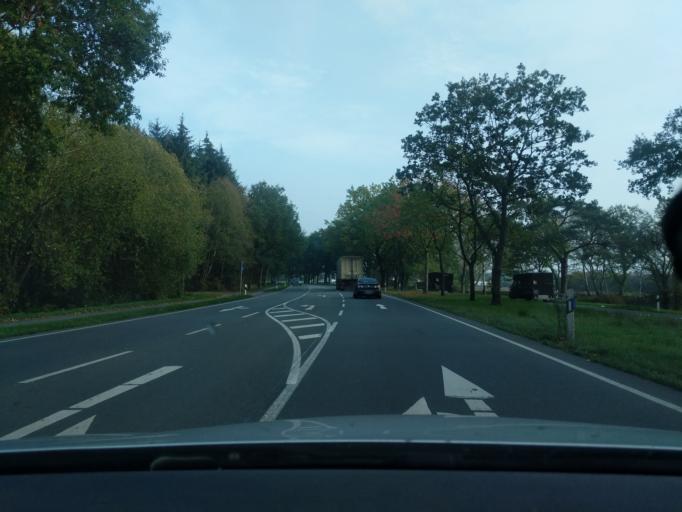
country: DE
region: Lower Saxony
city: Burweg
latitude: 53.6132
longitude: 9.2839
